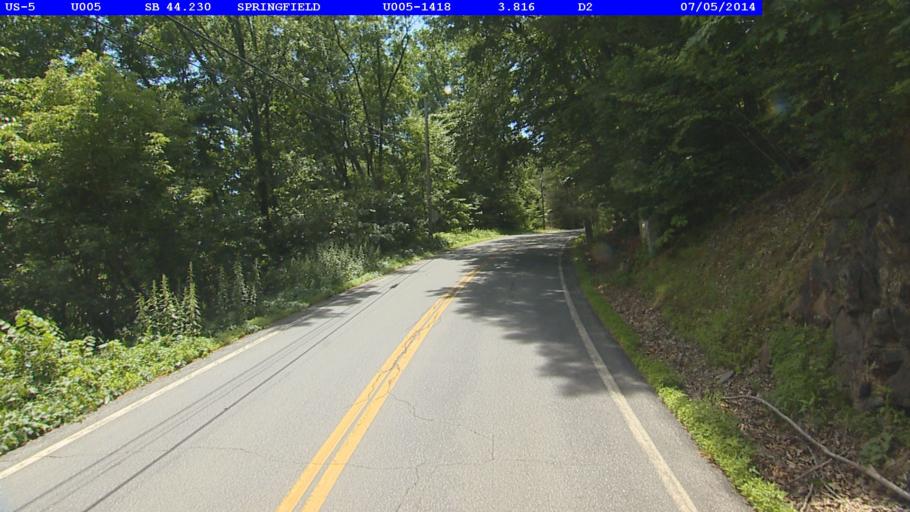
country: US
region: New Hampshire
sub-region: Sullivan County
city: Charlestown
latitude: 43.2693
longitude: -72.4179
